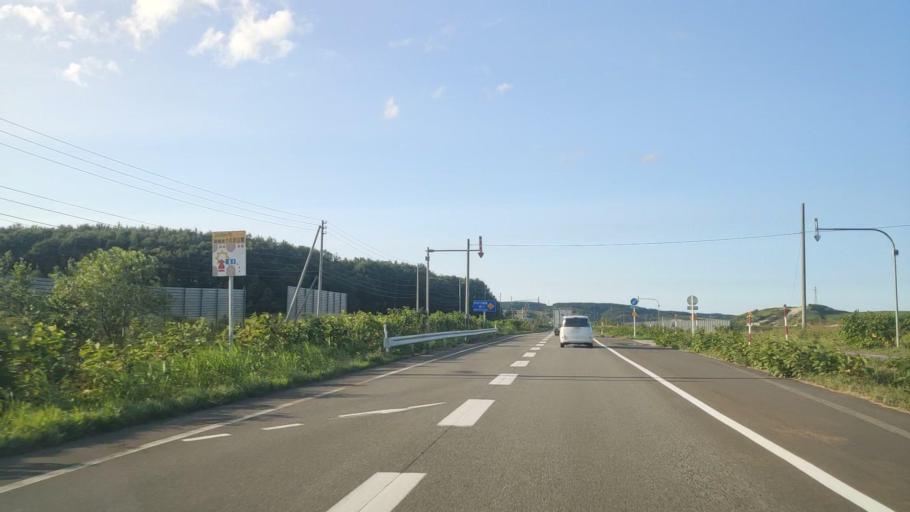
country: JP
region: Hokkaido
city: Wakkanai
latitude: 45.3234
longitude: 141.7195
